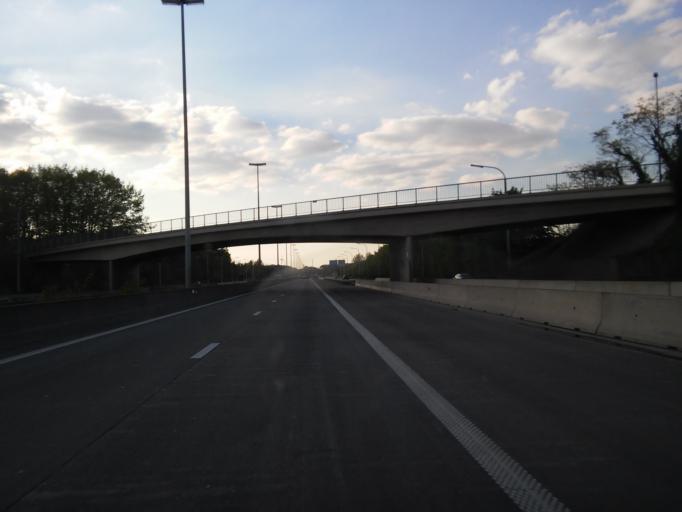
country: BE
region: Flanders
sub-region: Provincie Limburg
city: Tessenderlo
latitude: 51.0728
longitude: 5.1446
